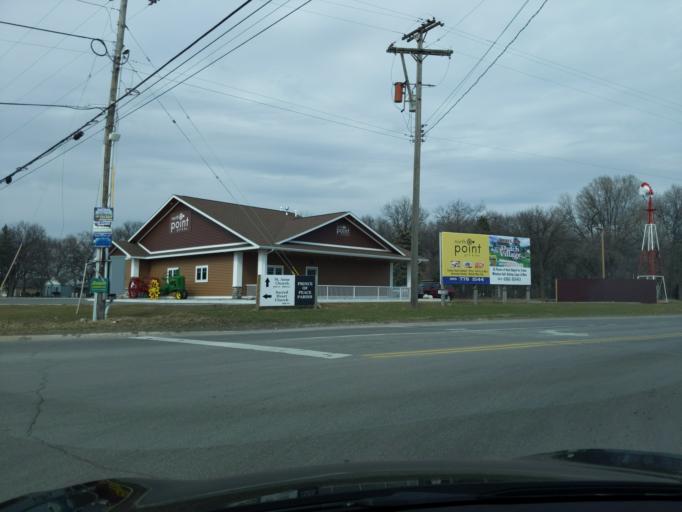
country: US
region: Michigan
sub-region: Bay County
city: Bay City
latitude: 43.6675
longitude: -83.9513
